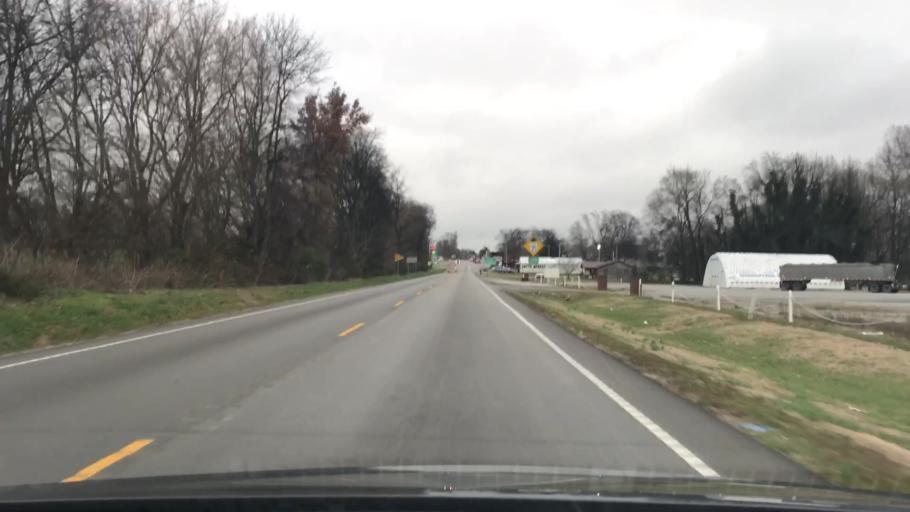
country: US
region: Kentucky
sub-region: Todd County
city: Guthrie
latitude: 36.6422
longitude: -87.2032
